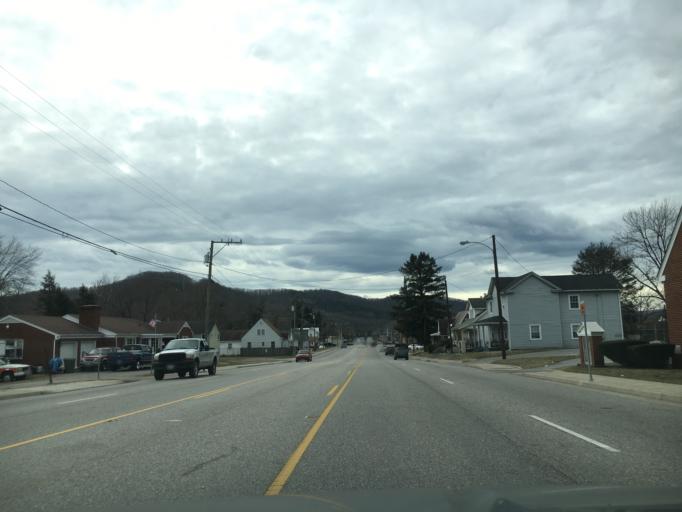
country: US
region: Virginia
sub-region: City of Waynesboro
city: Waynesboro
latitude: 38.0686
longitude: -78.8755
